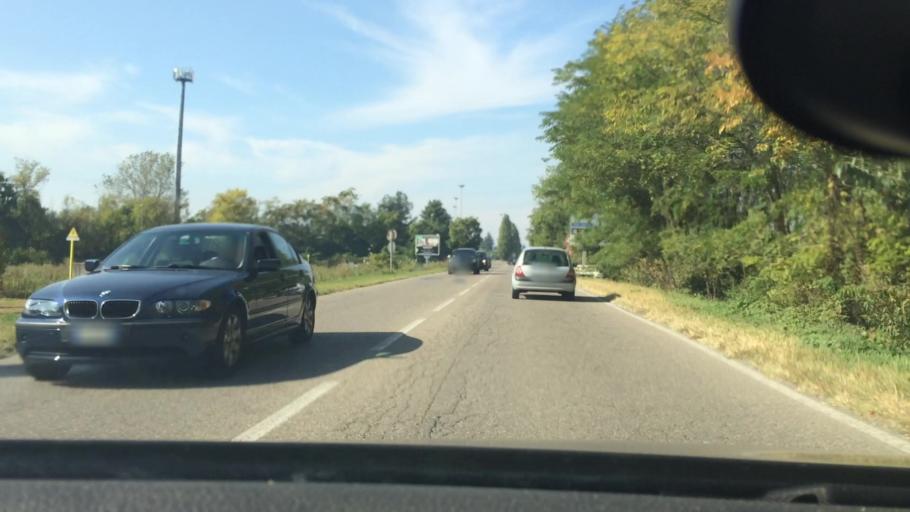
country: IT
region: Lombardy
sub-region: Citta metropolitana di Milano
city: Rescaldina
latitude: 45.6126
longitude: 8.9703
